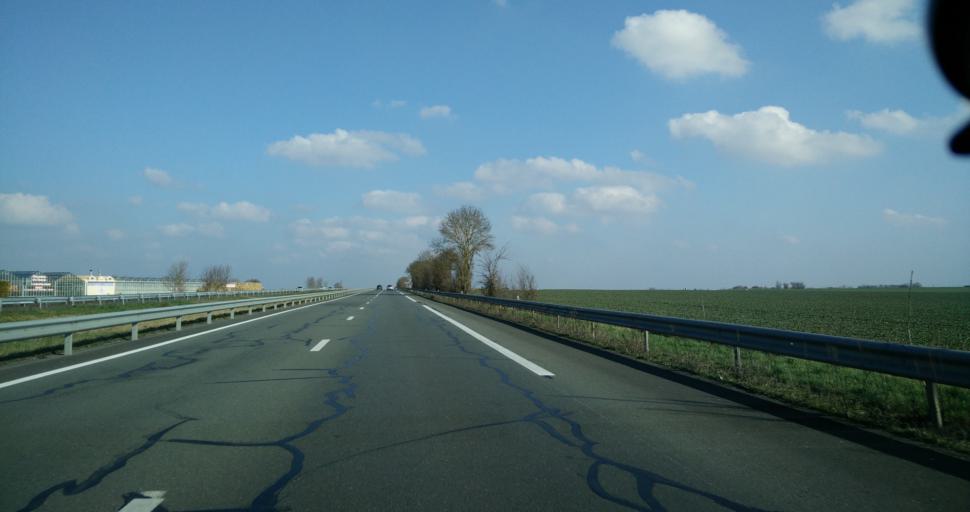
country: FR
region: Poitou-Charentes
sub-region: Departement de la Charente-Maritime
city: Verines
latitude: 46.2177
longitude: -0.9779
